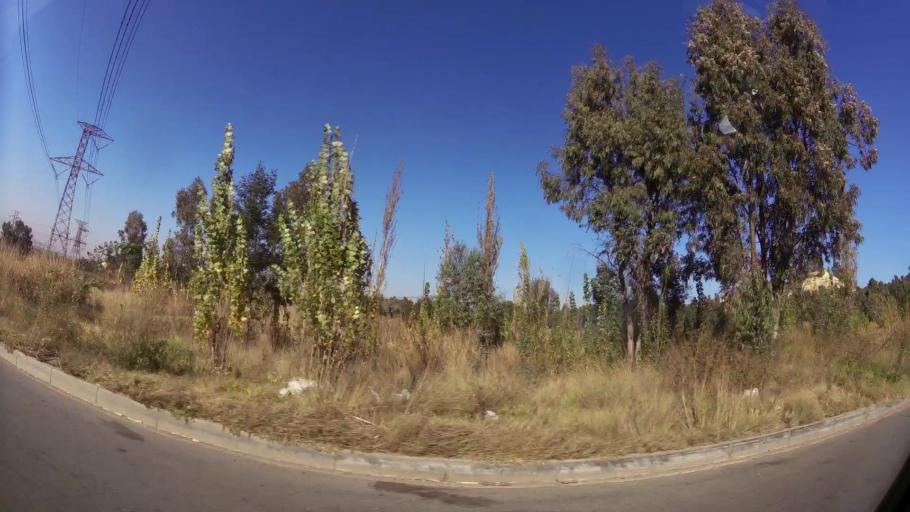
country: ZA
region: Gauteng
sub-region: City of Johannesburg Metropolitan Municipality
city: Johannesburg
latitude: -26.2276
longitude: 28.1050
